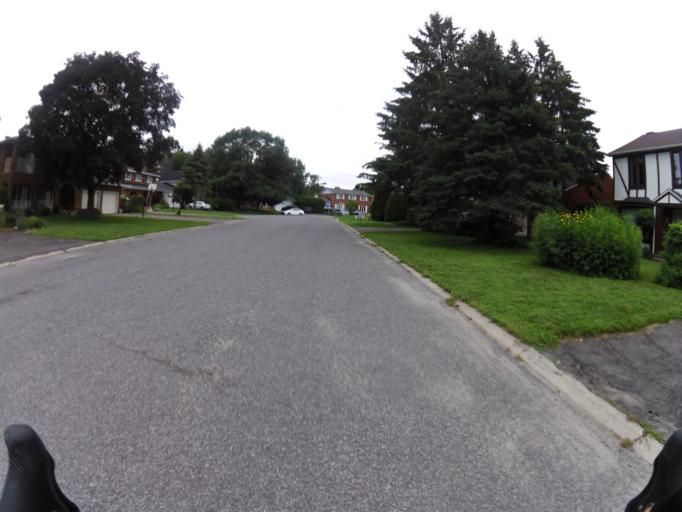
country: CA
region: Ontario
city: Ottawa
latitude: 45.3247
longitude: -75.7035
